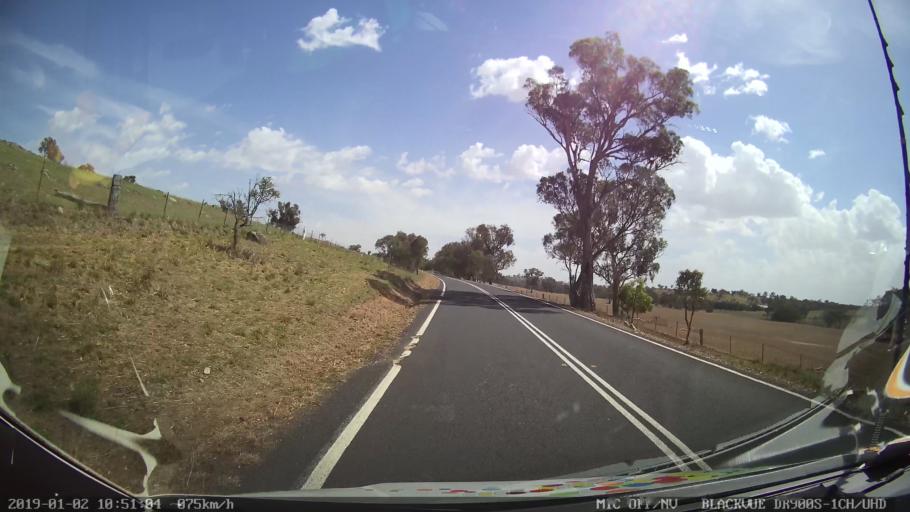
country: AU
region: New South Wales
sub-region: Cootamundra
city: Cootamundra
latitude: -34.7051
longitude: 148.2757
